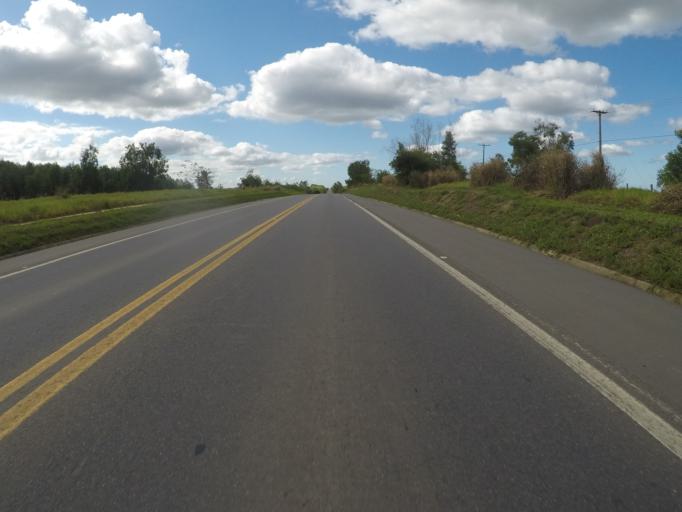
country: BR
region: Espirito Santo
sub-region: Linhares
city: Linhares
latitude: -19.1745
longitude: -40.0903
